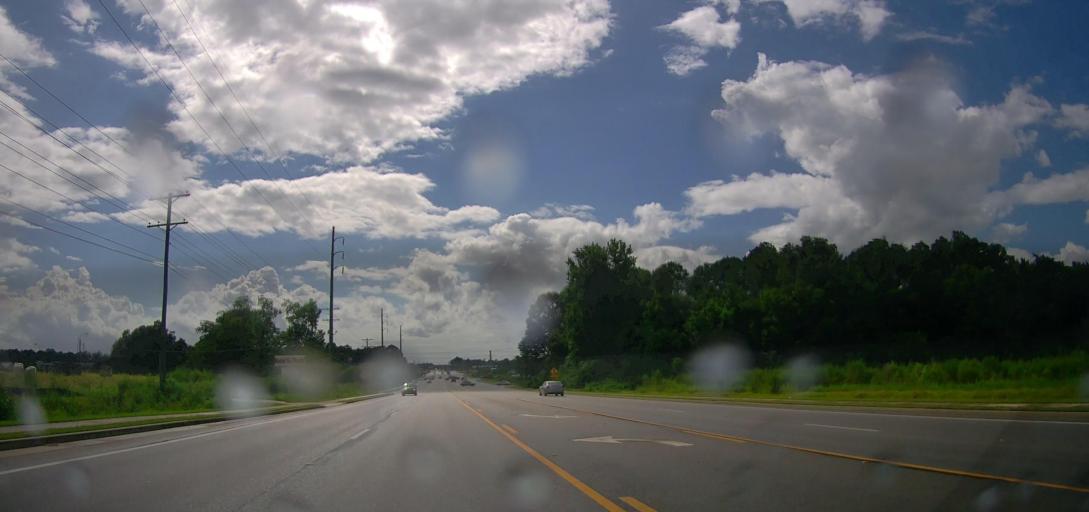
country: US
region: Georgia
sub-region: Coffee County
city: Douglas
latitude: 31.4875
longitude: -82.8426
